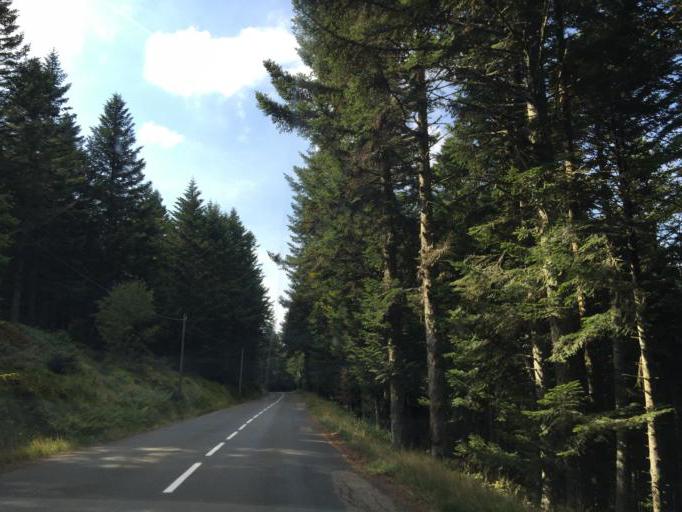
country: FR
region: Rhone-Alpes
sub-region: Departement de la Loire
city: Bourg-Argental
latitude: 45.3717
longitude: 4.5517
